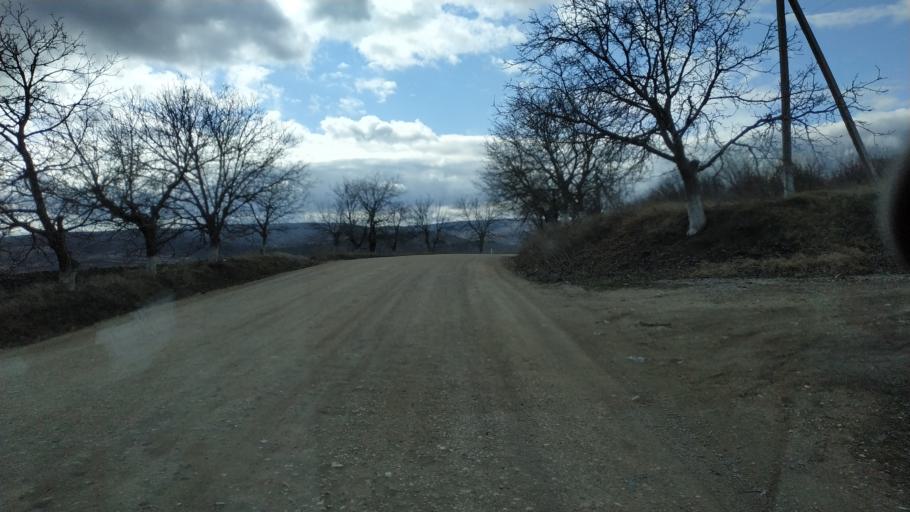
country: MD
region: Stinga Nistrului
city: Bucovat
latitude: 47.1940
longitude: 28.4878
